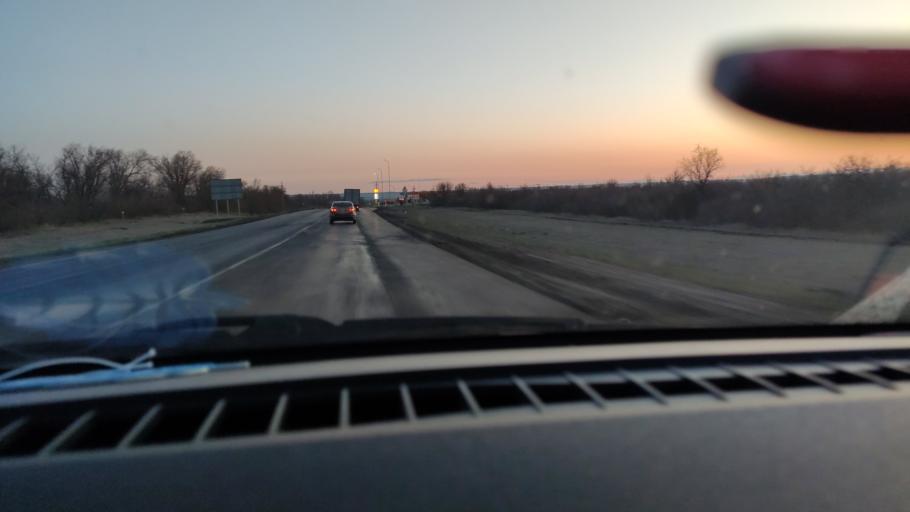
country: RU
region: Saratov
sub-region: Saratovskiy Rayon
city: Saratov
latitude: 51.6783
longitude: 46.0012
